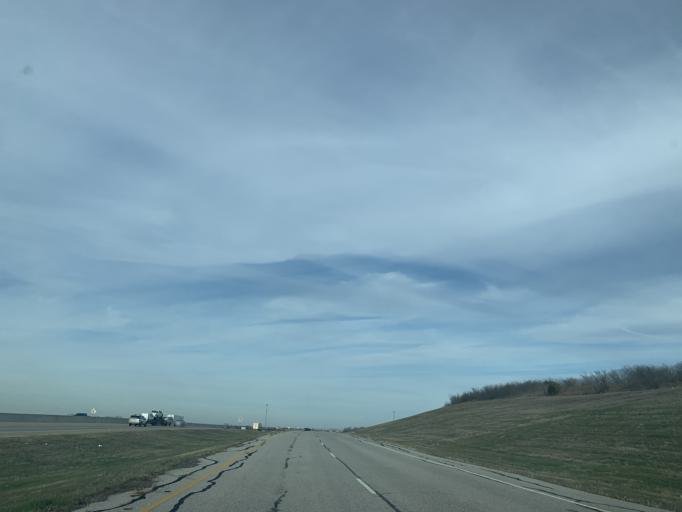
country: US
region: Texas
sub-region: Bell County
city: Salado
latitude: 30.8915
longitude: -97.5692
